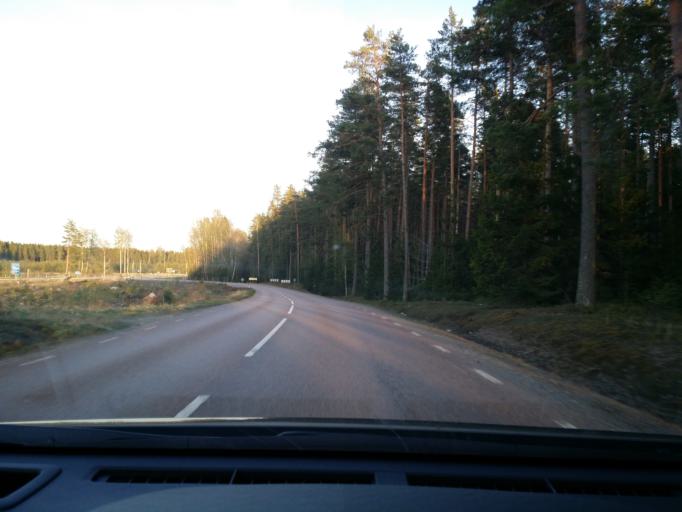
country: SE
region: Vaestmanland
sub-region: Sala Kommun
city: Sala
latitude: 59.8028
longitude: 16.5542
